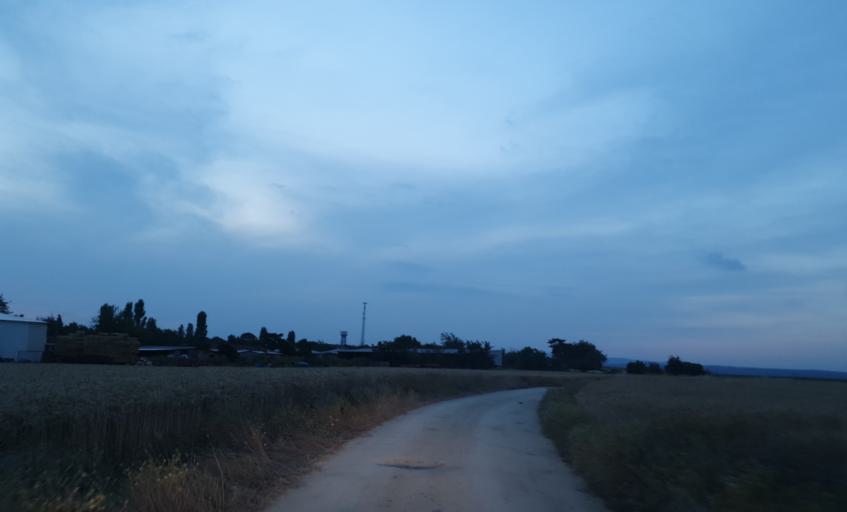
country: TR
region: Kirklareli
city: Vize
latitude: 41.5147
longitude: 27.7448
